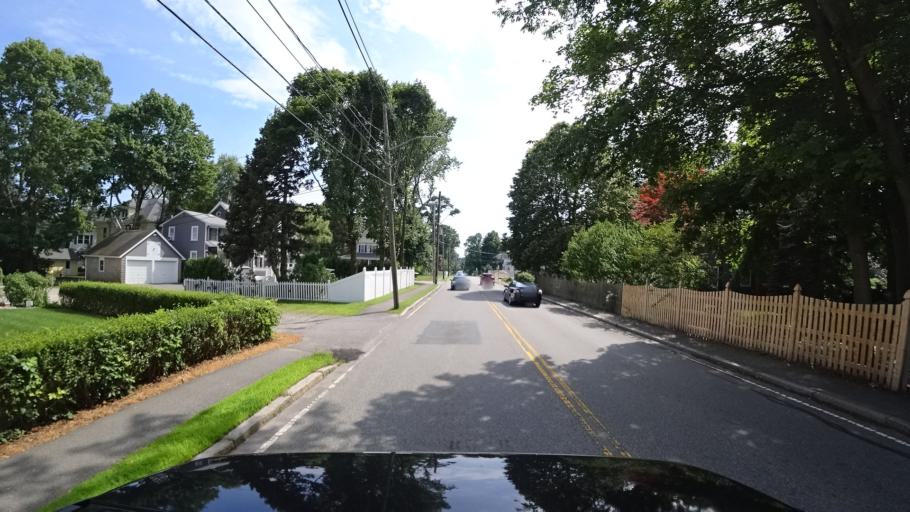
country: US
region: Massachusetts
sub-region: Norfolk County
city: Dedham
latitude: 42.2440
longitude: -71.1765
